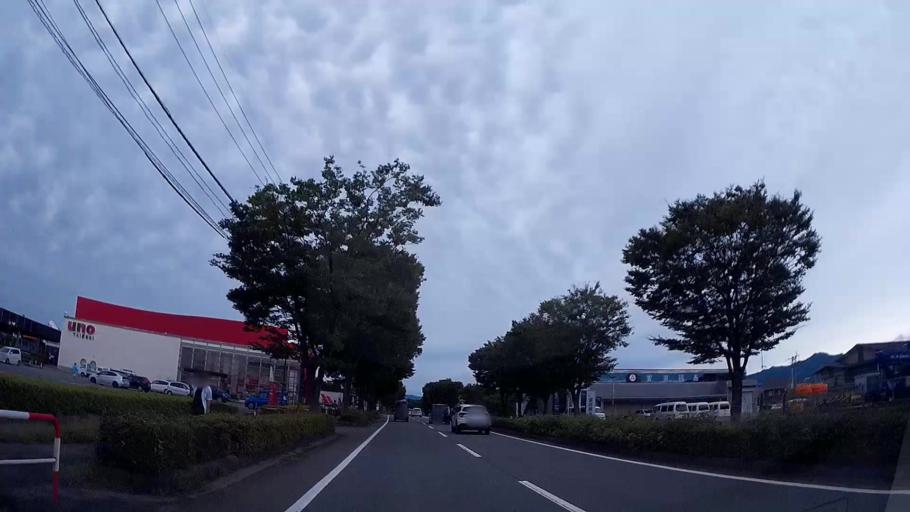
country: JP
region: Kumamoto
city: Ozu
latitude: 32.8881
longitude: 130.8543
